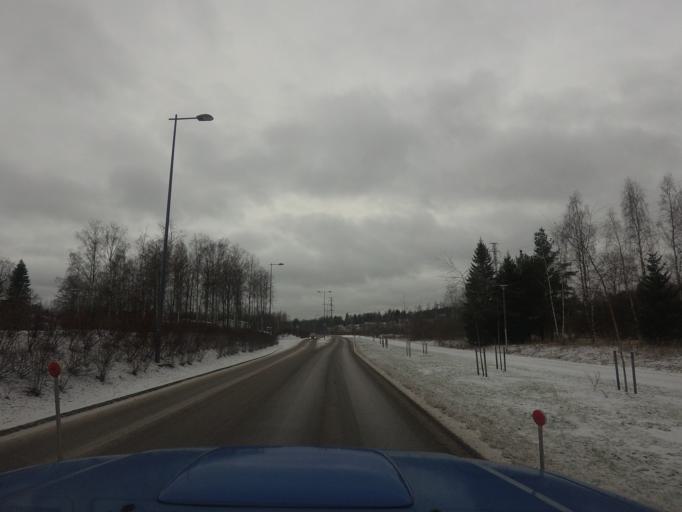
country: FI
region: Uusimaa
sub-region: Helsinki
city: Espoo
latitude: 60.1700
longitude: 24.6535
